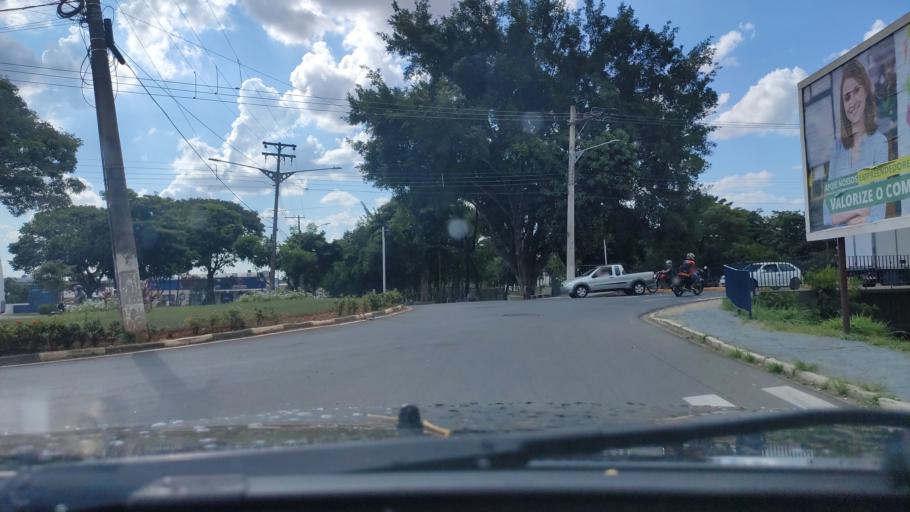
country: BR
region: Sao Paulo
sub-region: Itapira
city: Itapira
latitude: -22.4298
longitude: -46.8222
